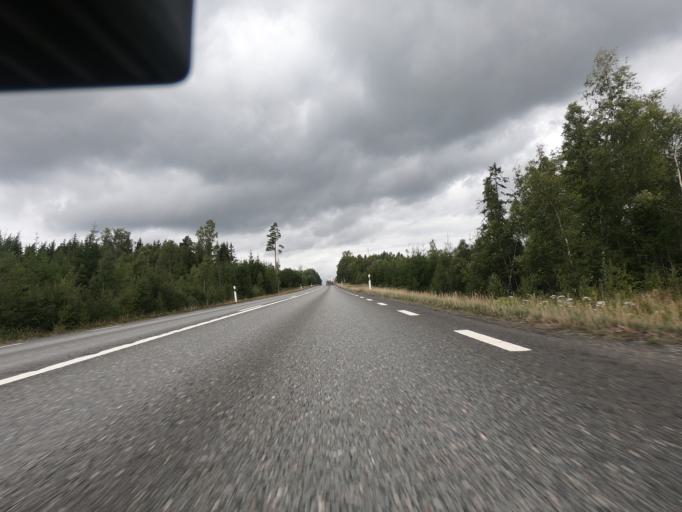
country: SE
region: Joenkoeping
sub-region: Savsjo Kommun
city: Vrigstad
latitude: 57.4163
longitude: 14.3375
